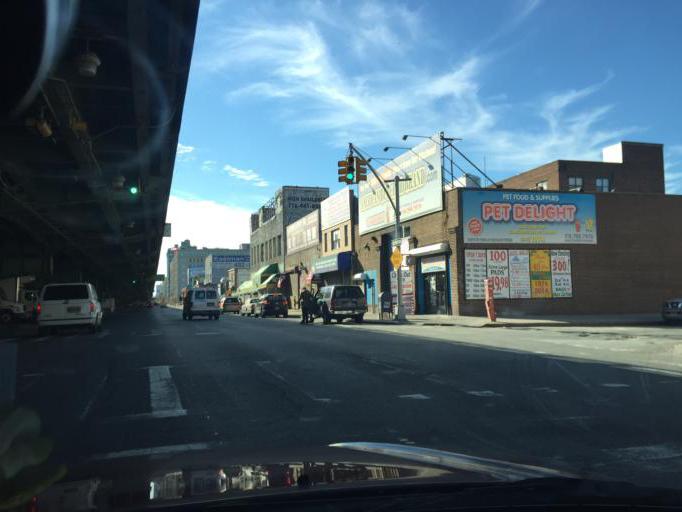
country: US
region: New York
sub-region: Kings County
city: Brooklyn
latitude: 40.6619
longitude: -74.0000
